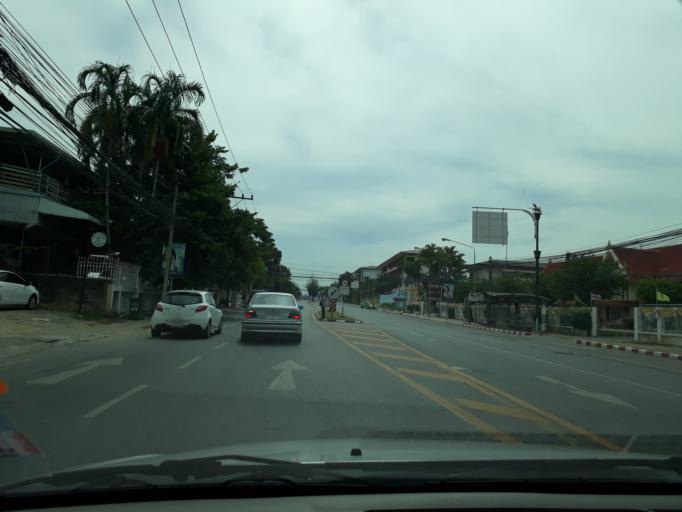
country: TH
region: Khon Kaen
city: Khon Kaen
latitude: 16.4380
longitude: 102.8397
